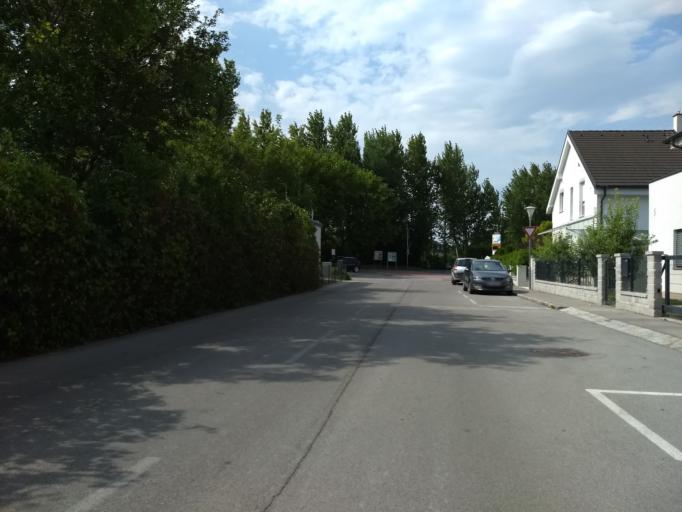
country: AT
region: Lower Austria
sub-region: Politischer Bezirk Modling
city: Neu-Guntramsdorf
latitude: 48.0580
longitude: 16.3187
